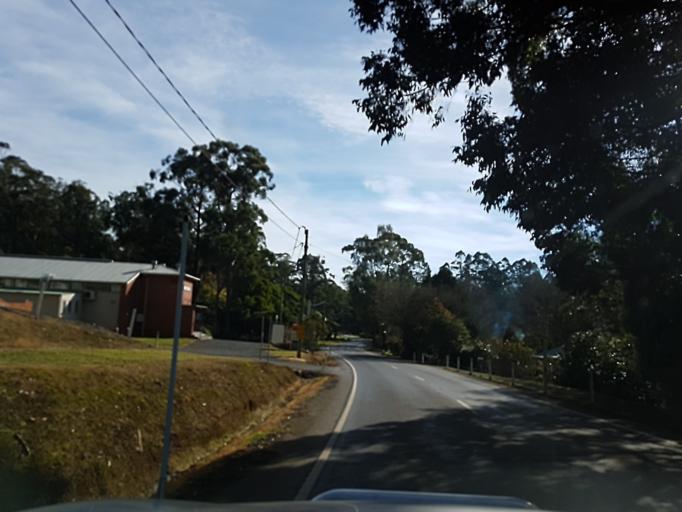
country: AU
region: Victoria
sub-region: Yarra Ranges
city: Healesville
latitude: -37.5383
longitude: 145.4744
